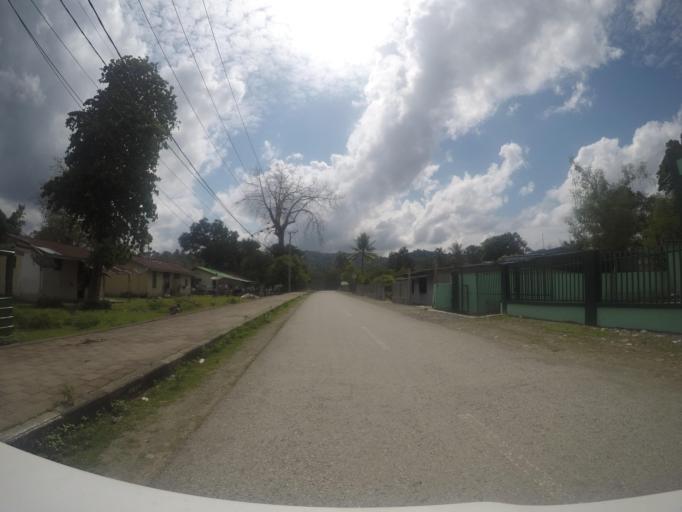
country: TL
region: Viqueque
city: Viqueque
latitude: -8.8562
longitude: 126.3646
